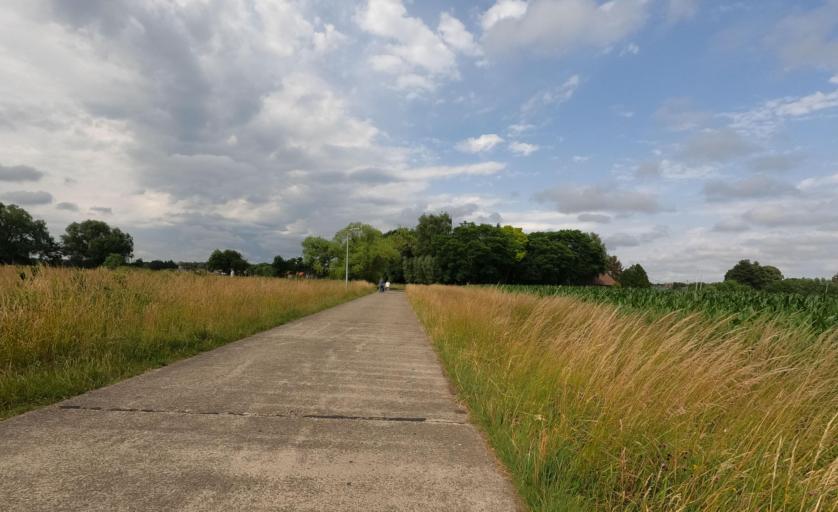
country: BE
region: Flanders
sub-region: Provincie Antwerpen
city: Heist-op-den-Berg
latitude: 51.1102
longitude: 4.7221
